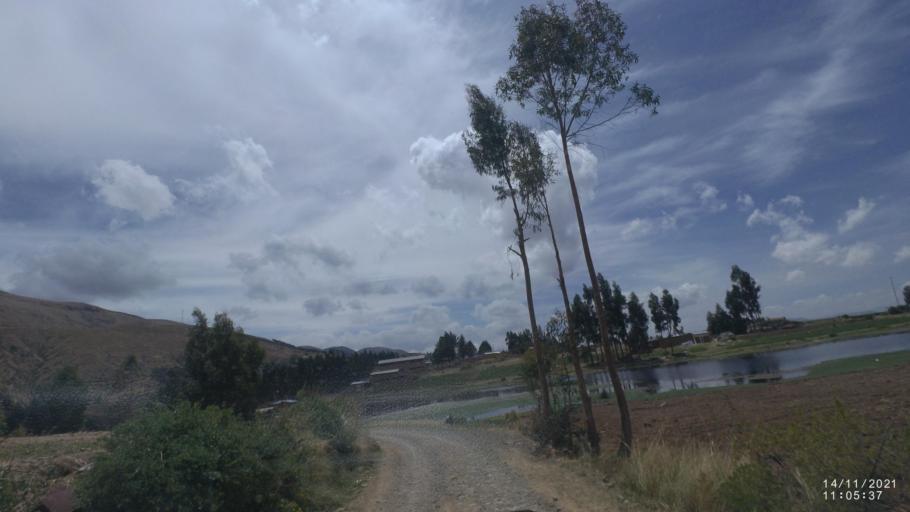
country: BO
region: Cochabamba
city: Cochabamba
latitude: -17.3331
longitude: -66.0567
